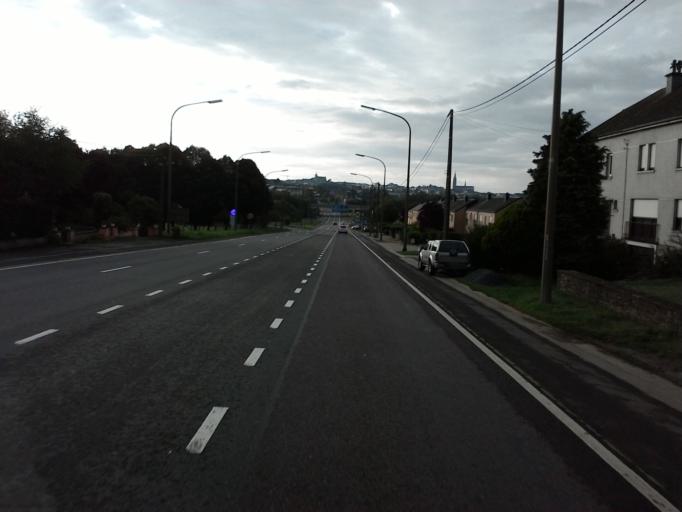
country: BE
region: Wallonia
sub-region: Province du Luxembourg
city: Arlon
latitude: 49.7018
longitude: 5.8067
